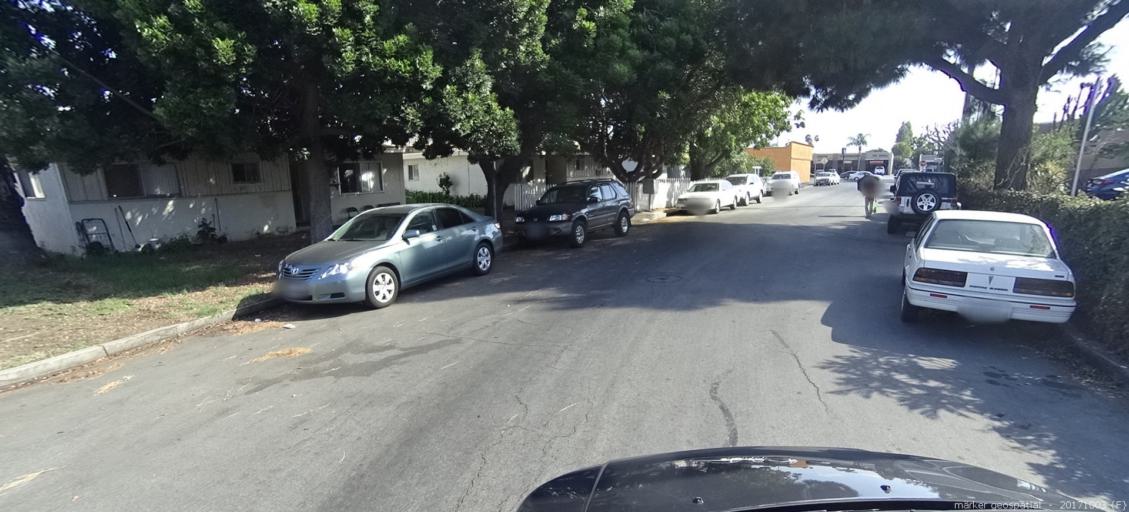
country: US
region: California
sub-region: Orange County
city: Garden Grove
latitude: 33.7749
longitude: -117.9718
